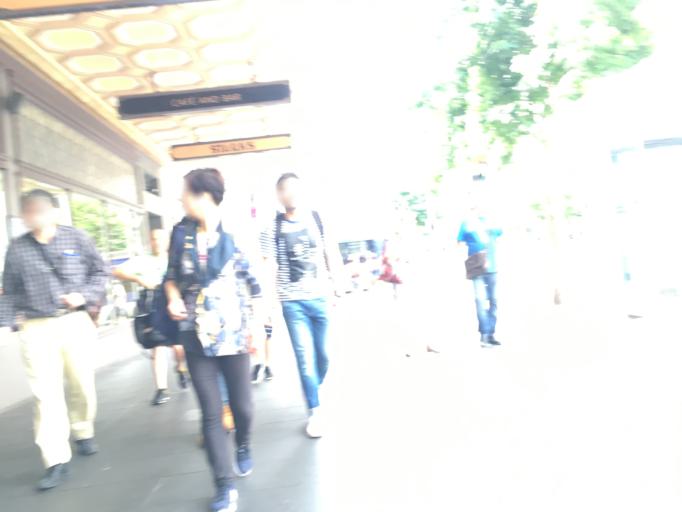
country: NZ
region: Auckland
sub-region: Auckland
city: Auckland
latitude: -36.8512
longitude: 174.7646
